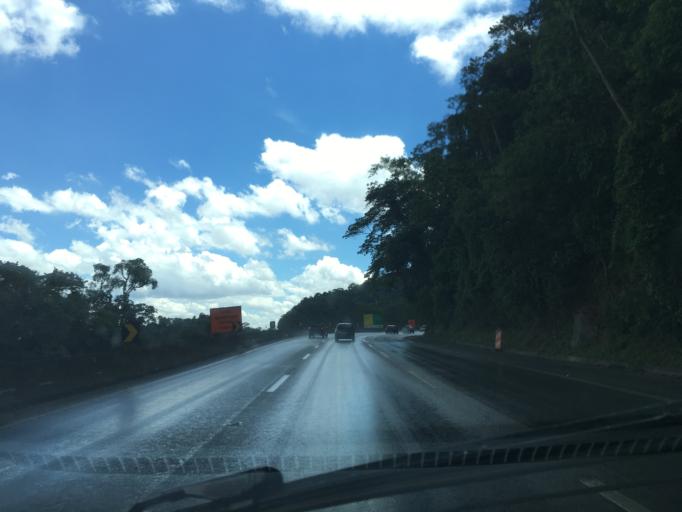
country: BR
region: Sao Paulo
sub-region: Mairipora
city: Mairipora
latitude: -23.3746
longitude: -46.5604
